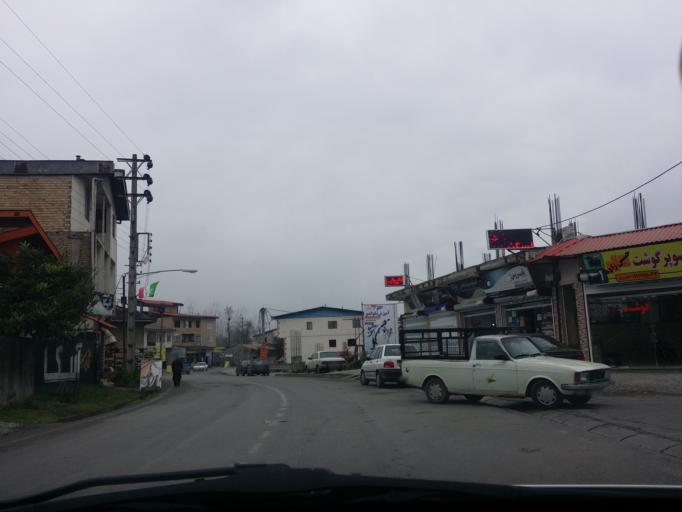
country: IR
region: Mazandaran
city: Chalus
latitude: 36.6631
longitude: 51.3948
